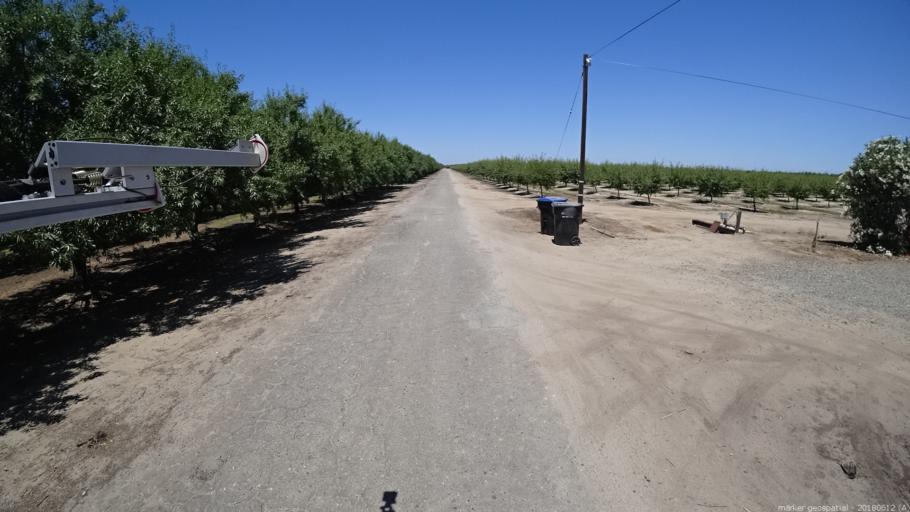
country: US
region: California
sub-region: Madera County
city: Chowchilla
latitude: 37.0722
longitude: -120.2704
